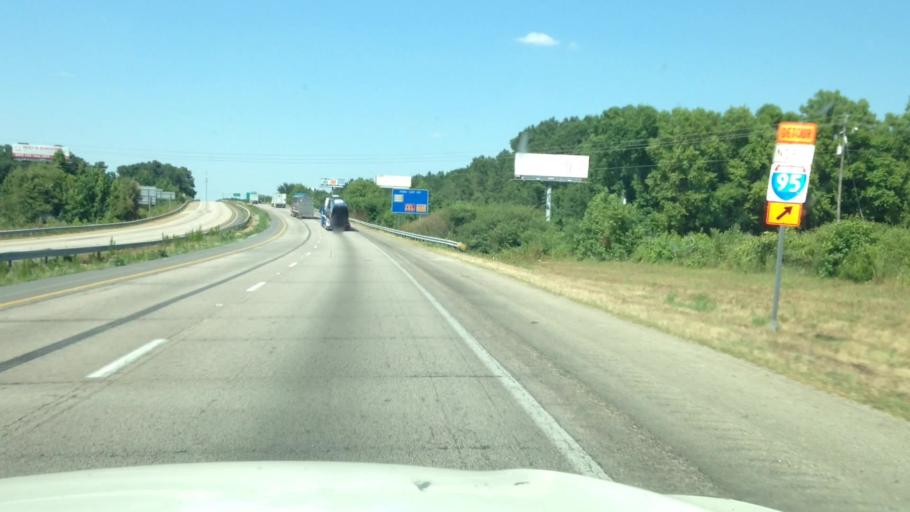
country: US
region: North Carolina
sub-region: Johnston County
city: Kenly
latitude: 35.5855
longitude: -78.1373
